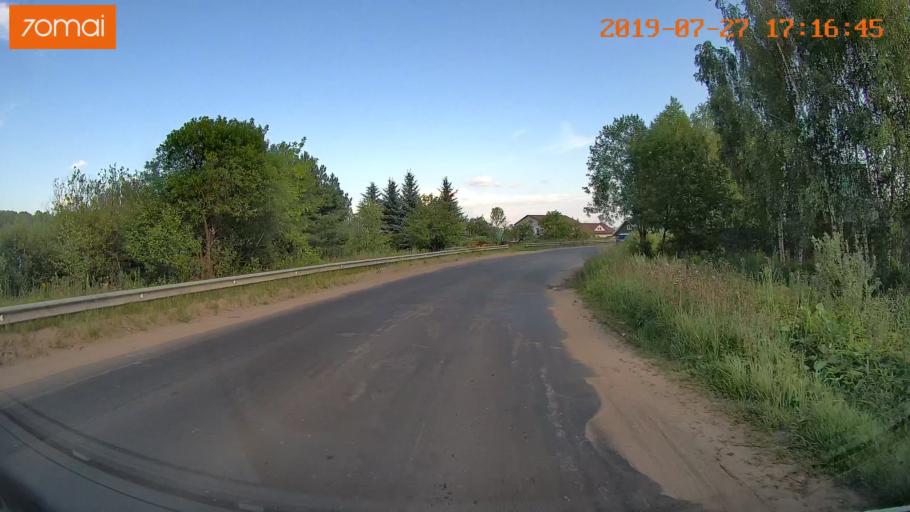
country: RU
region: Ivanovo
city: Novo-Talitsy
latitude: 57.0430
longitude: 40.8894
